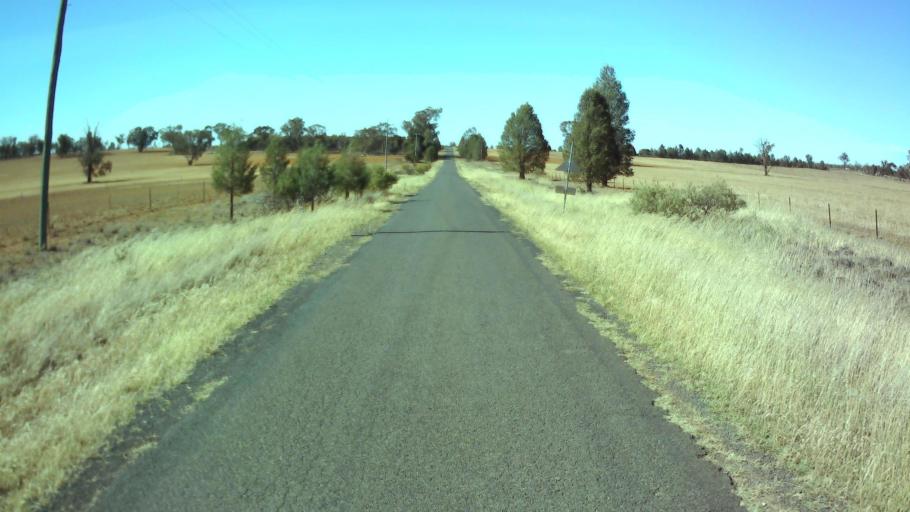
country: AU
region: New South Wales
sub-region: Weddin
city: Grenfell
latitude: -33.7609
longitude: 147.8295
